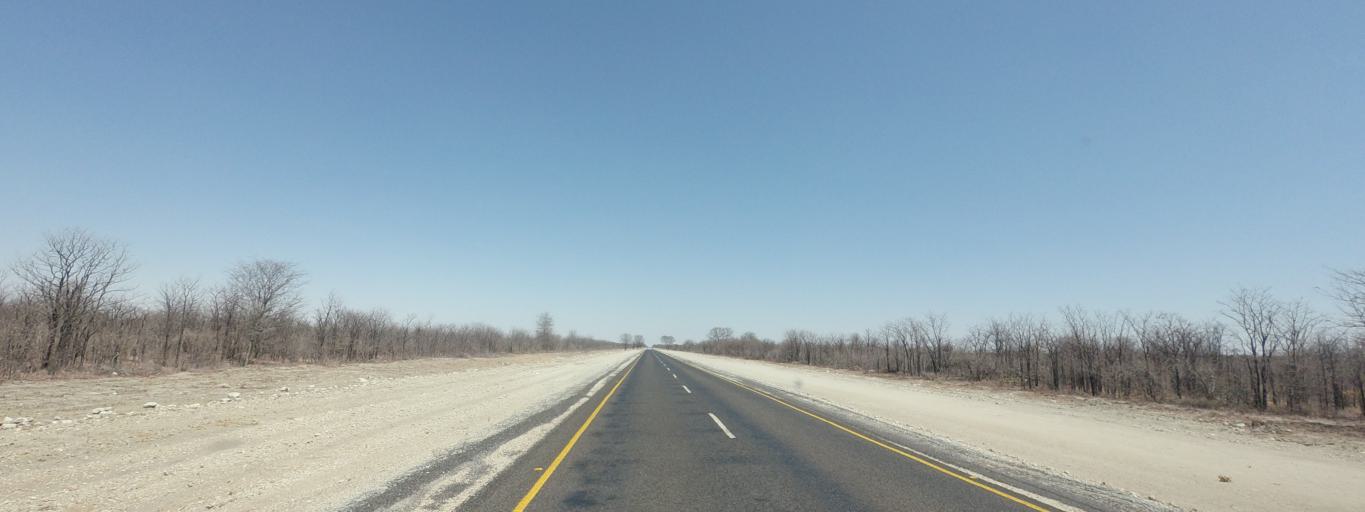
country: BW
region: North East
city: Dukwe
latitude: -20.3978
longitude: 26.3592
